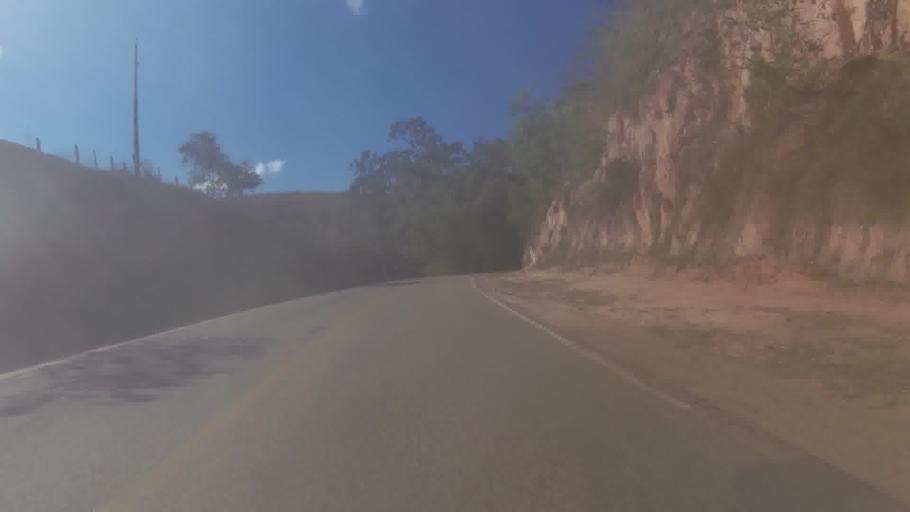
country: BR
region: Espirito Santo
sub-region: Cachoeiro De Itapemirim
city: Cachoeiro de Itapemirim
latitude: -21.0427
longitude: -41.0747
